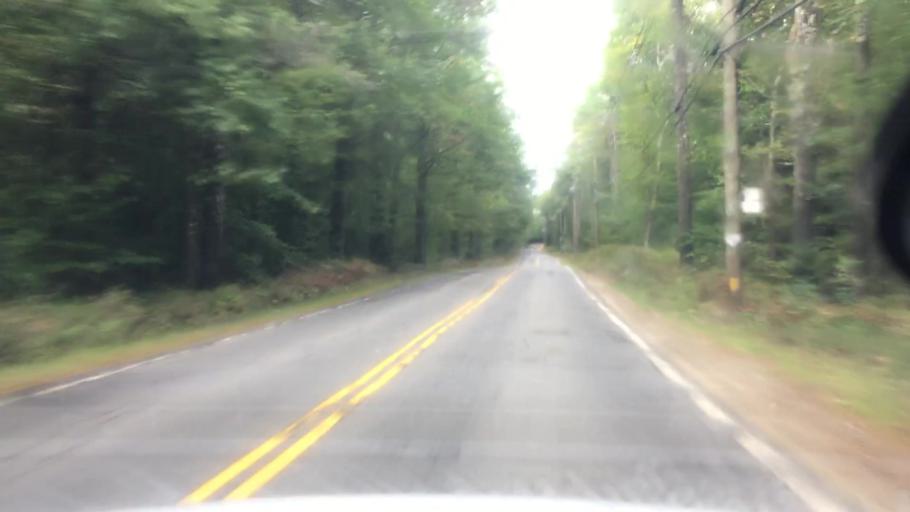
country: US
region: New Hampshire
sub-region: Carroll County
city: Wakefield
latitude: 43.5745
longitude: -71.0228
